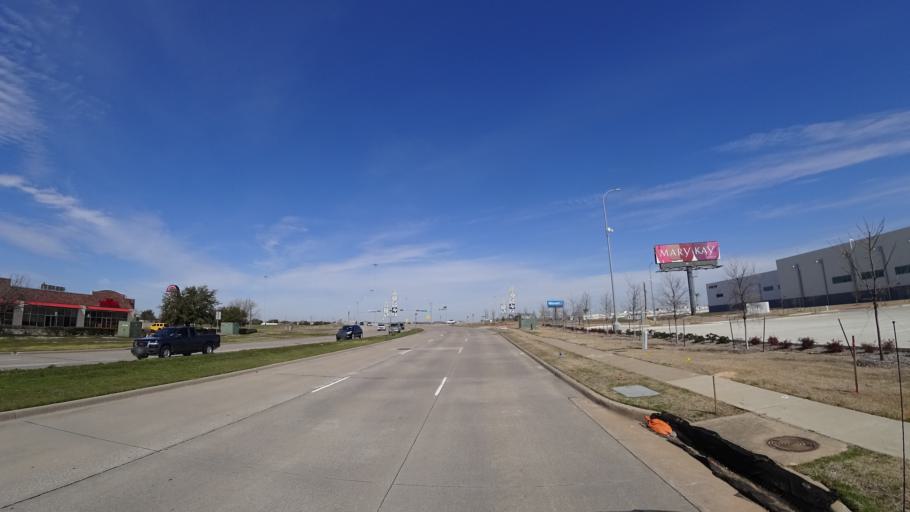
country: US
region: Texas
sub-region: Denton County
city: Lewisville
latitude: 32.9981
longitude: -96.9931
